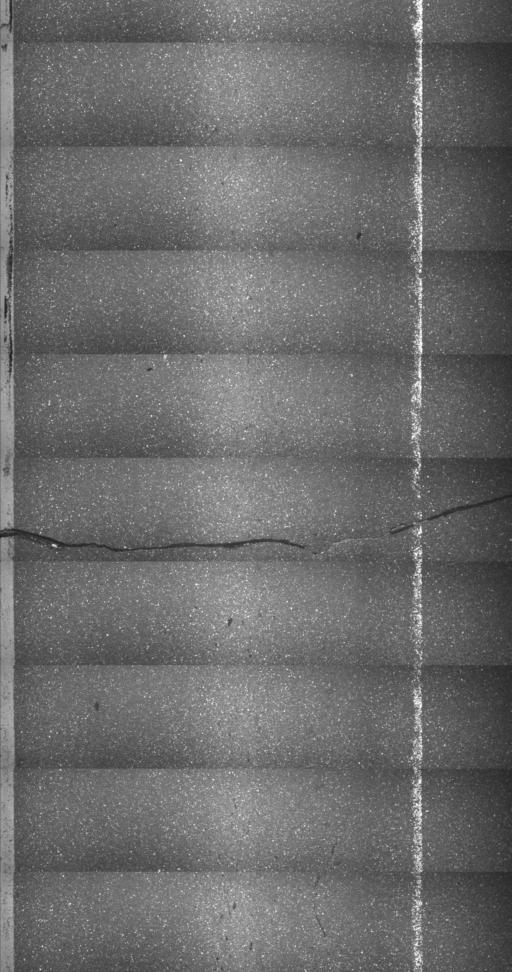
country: US
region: Vermont
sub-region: Orange County
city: Williamstown
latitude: 44.1189
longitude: -72.5412
